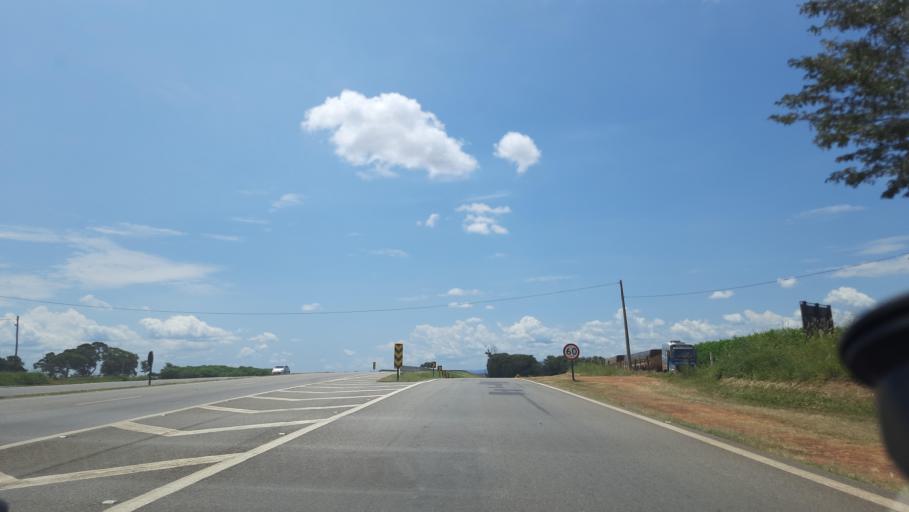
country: BR
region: Sao Paulo
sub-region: Mococa
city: Mococa
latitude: -21.5219
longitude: -47.0275
